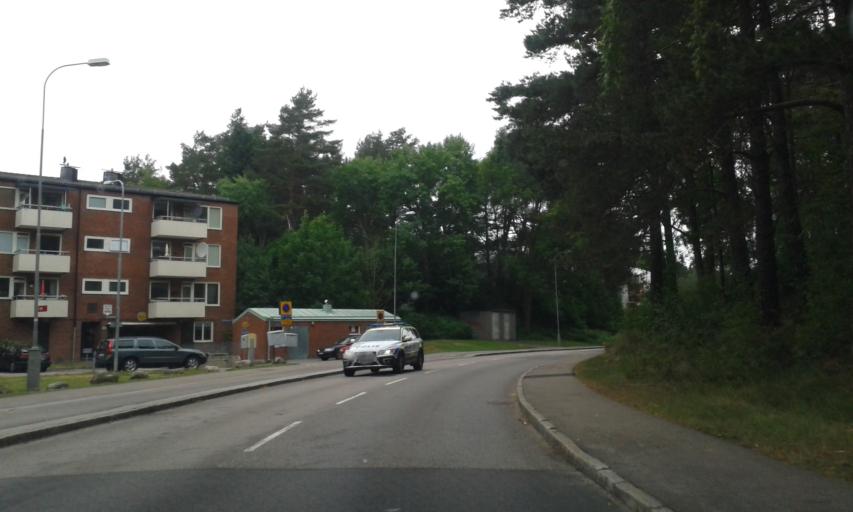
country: SE
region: Vaestra Goetaland
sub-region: Goteborg
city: Eriksbo
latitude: 57.7542
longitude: 12.0274
